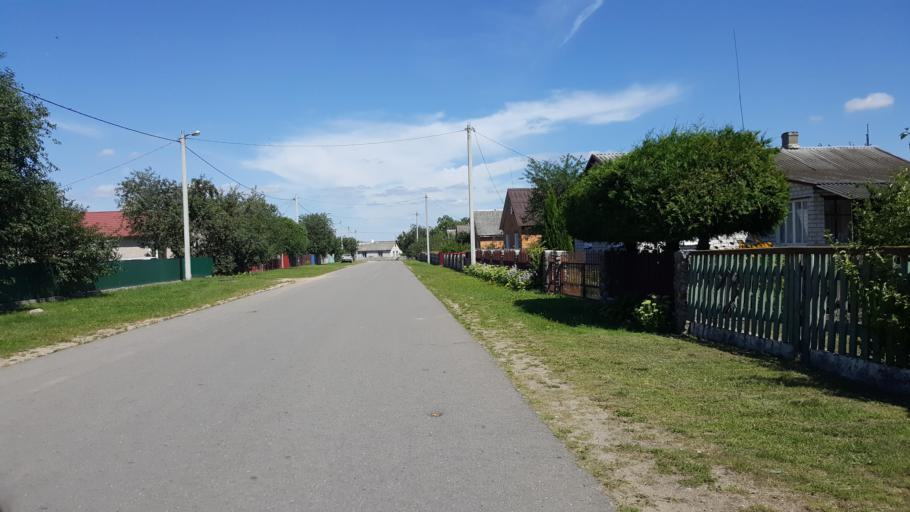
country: BY
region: Brest
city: Charnawchytsy
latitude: 52.3456
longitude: 23.6091
